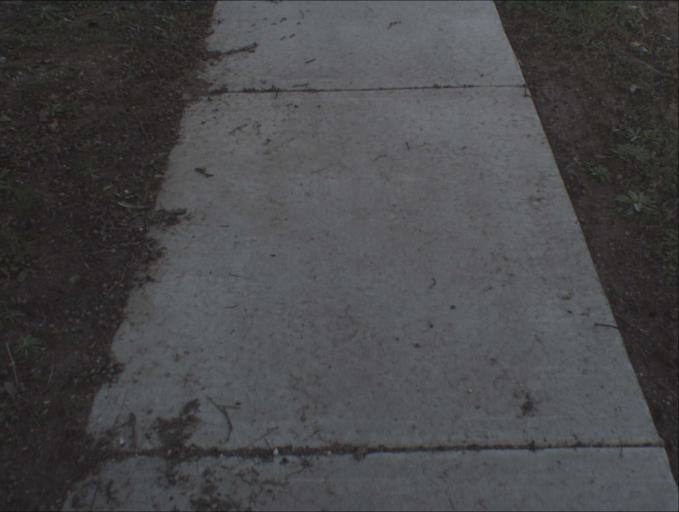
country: AU
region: Queensland
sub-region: Logan
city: Waterford West
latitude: -27.6904
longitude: 153.1215
